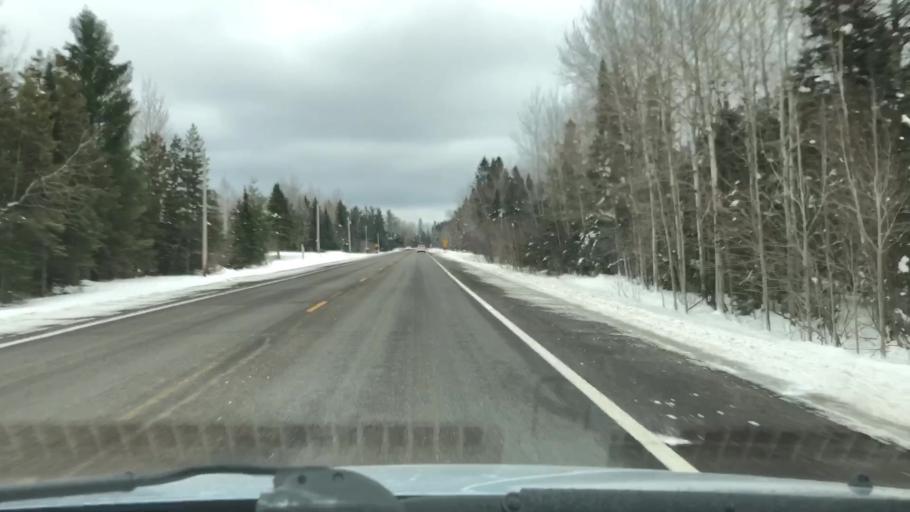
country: US
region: Minnesota
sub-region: Carlton County
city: Esko
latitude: 46.6888
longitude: -92.3648
